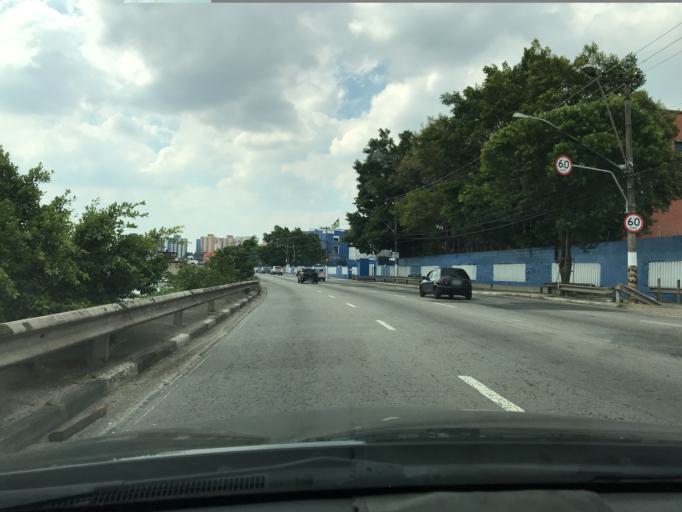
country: BR
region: Sao Paulo
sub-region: Sao Caetano Do Sul
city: Sao Caetano do Sul
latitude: -23.6119
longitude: -46.5441
